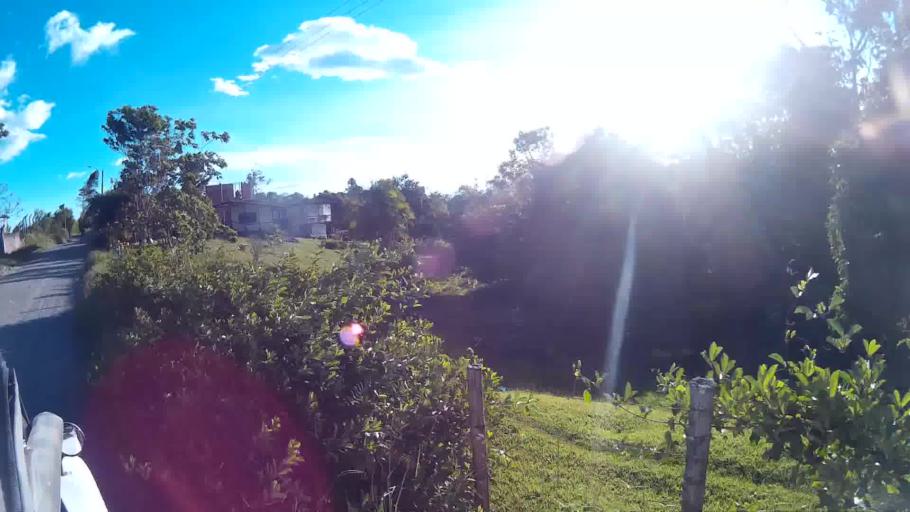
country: CO
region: Quindio
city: Filandia
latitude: 4.7125
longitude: -75.6480
